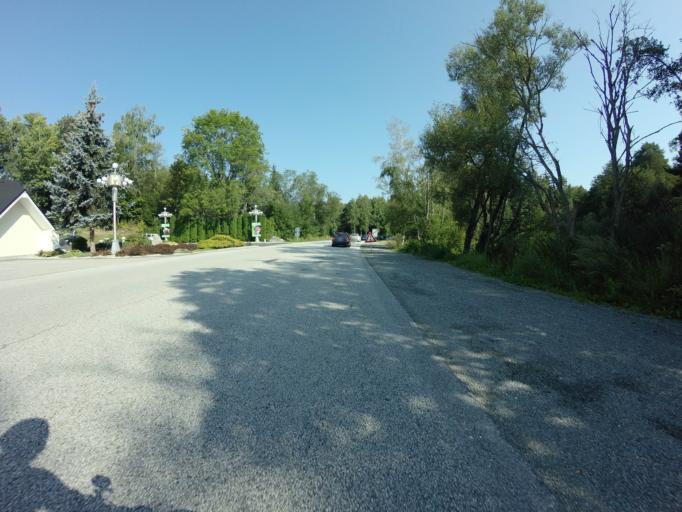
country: CZ
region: Jihocesky
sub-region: Okres Cesky Krumlov
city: Vyssi Brod
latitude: 48.5779
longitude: 14.3182
